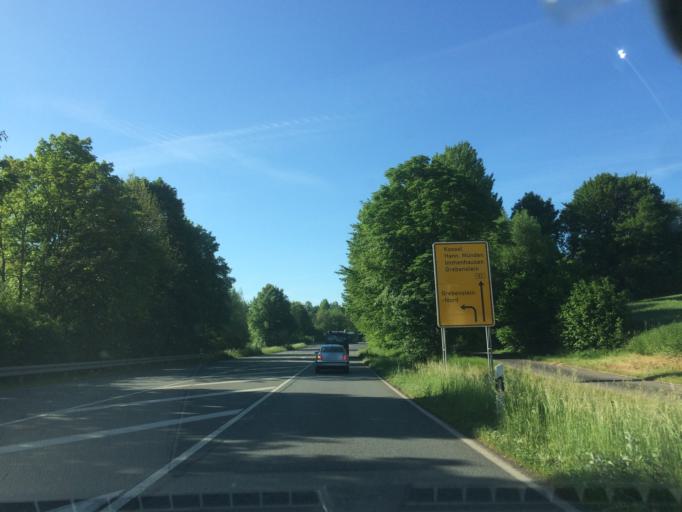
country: DE
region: Hesse
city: Grebenstein
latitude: 51.4556
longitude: 9.4095
